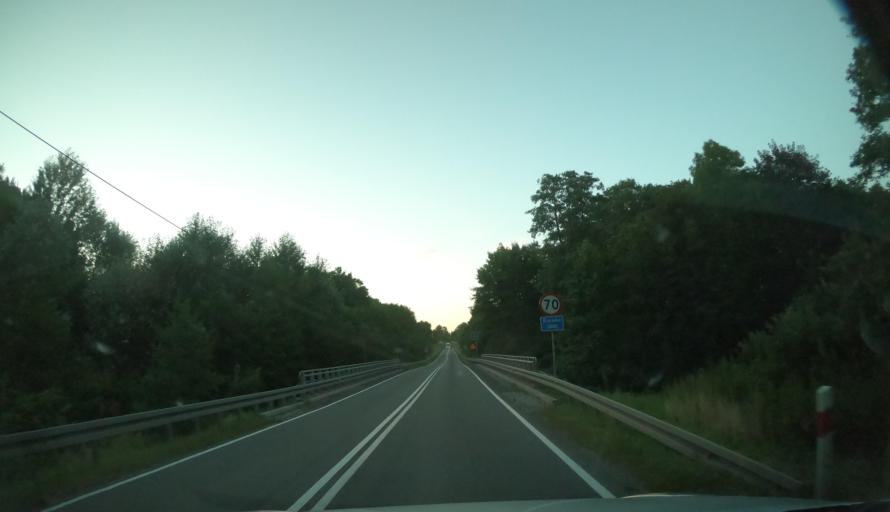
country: PL
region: Kujawsko-Pomorskie
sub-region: Powiat bydgoski
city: Koronowo
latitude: 53.3589
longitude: 17.8618
